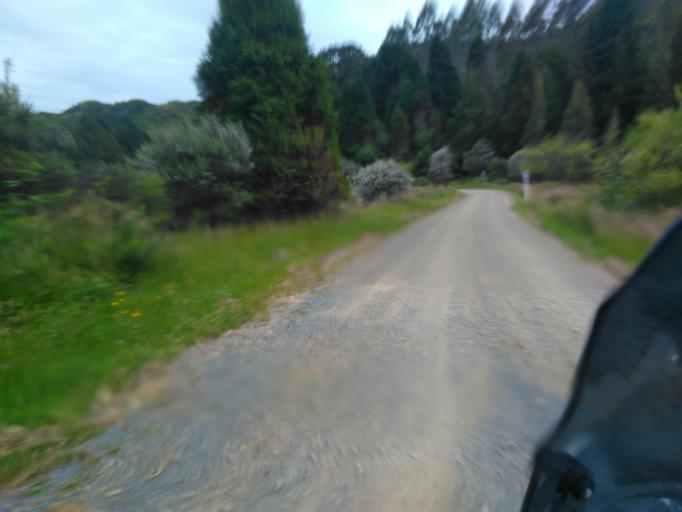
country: NZ
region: Bay of Plenty
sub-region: Opotiki District
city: Opotiki
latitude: -38.1092
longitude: 177.5065
